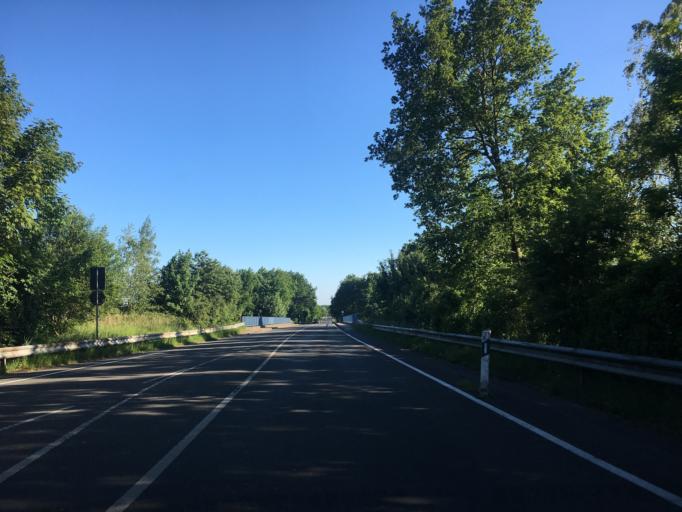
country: DE
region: North Rhine-Westphalia
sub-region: Regierungsbezirk Munster
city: Senden
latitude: 51.9120
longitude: 7.5291
